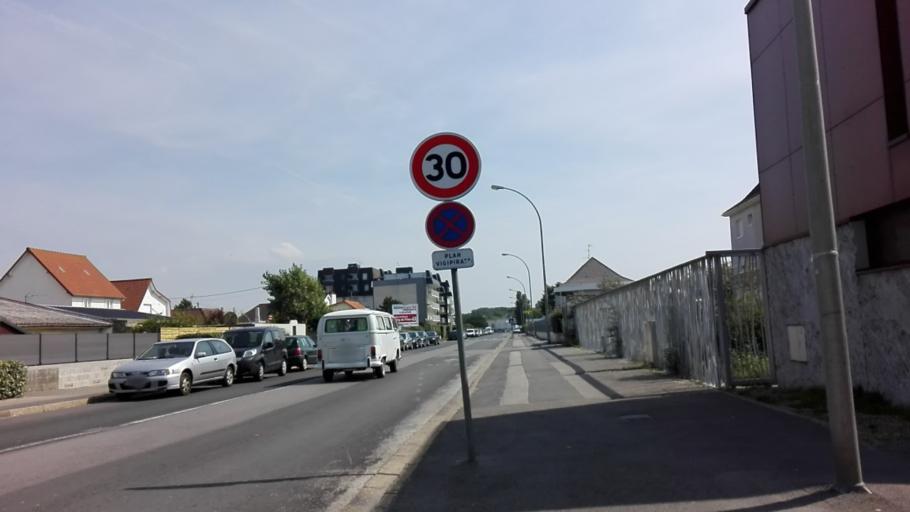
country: FR
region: Nord-Pas-de-Calais
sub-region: Departement du Pas-de-Calais
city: Berck-Plage
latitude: 50.4002
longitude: 1.5645
